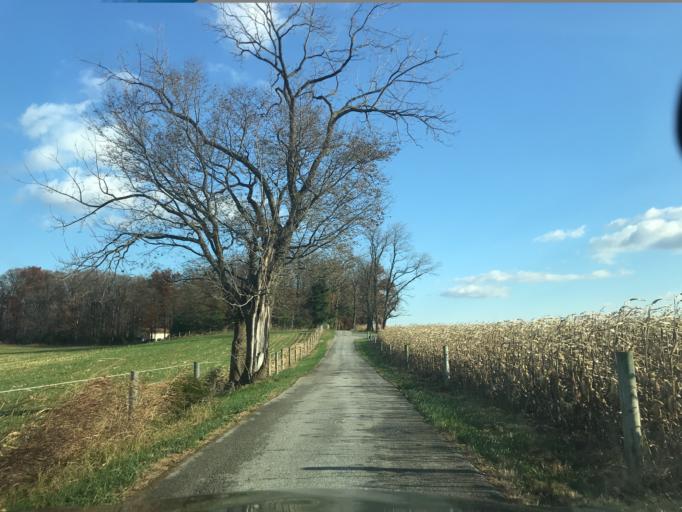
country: US
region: Maryland
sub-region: Carroll County
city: Taneytown
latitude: 39.6292
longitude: -77.0954
